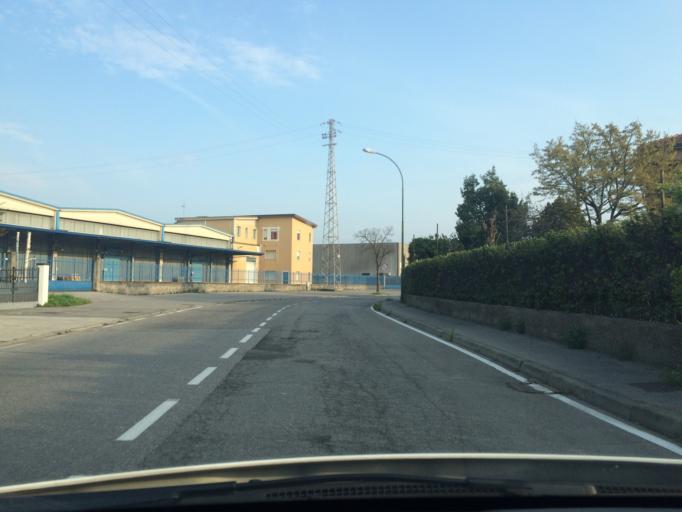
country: IT
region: Lombardy
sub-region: Provincia di Brescia
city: Flero
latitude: 45.4945
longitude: 10.1661
